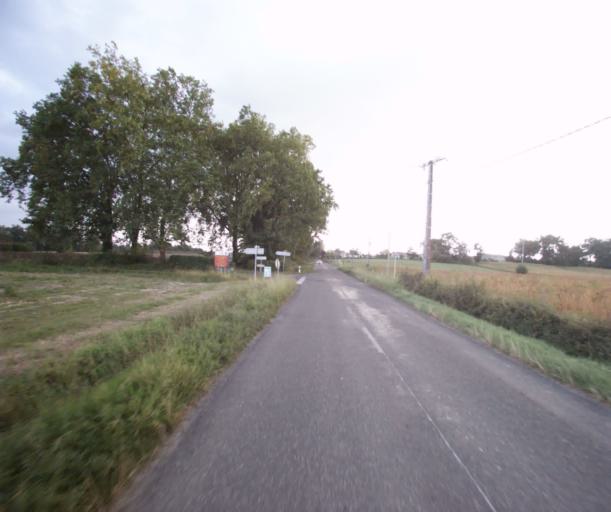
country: FR
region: Midi-Pyrenees
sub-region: Departement du Gers
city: Cazaubon
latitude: 43.9216
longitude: -0.0774
